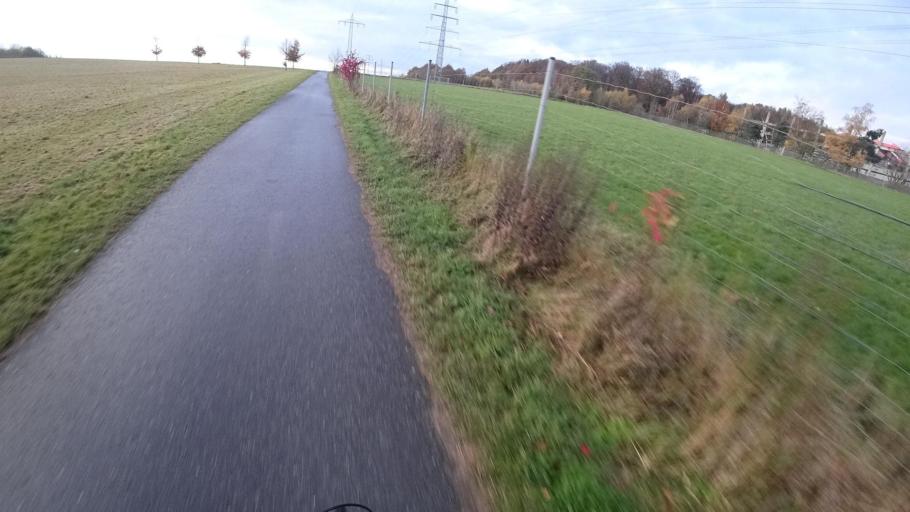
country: DE
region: Rheinland-Pfalz
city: Halsenbach
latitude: 50.1652
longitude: 7.5606
